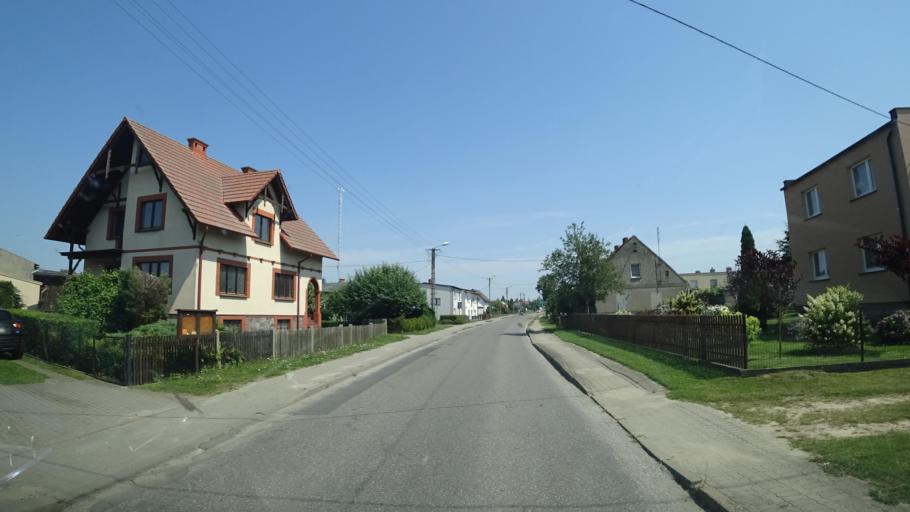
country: PL
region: Pomeranian Voivodeship
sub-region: Powiat chojnicki
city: Brusy
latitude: 53.8733
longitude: 17.6804
